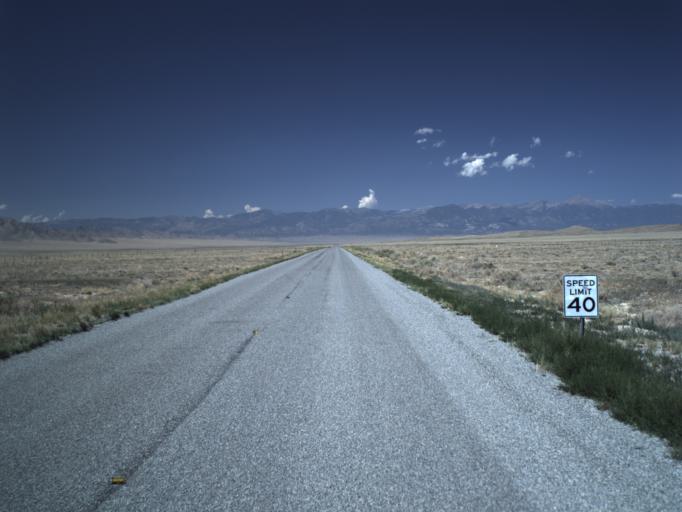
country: US
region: Utah
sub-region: Beaver County
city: Milford
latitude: 39.0596
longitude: -113.7584
